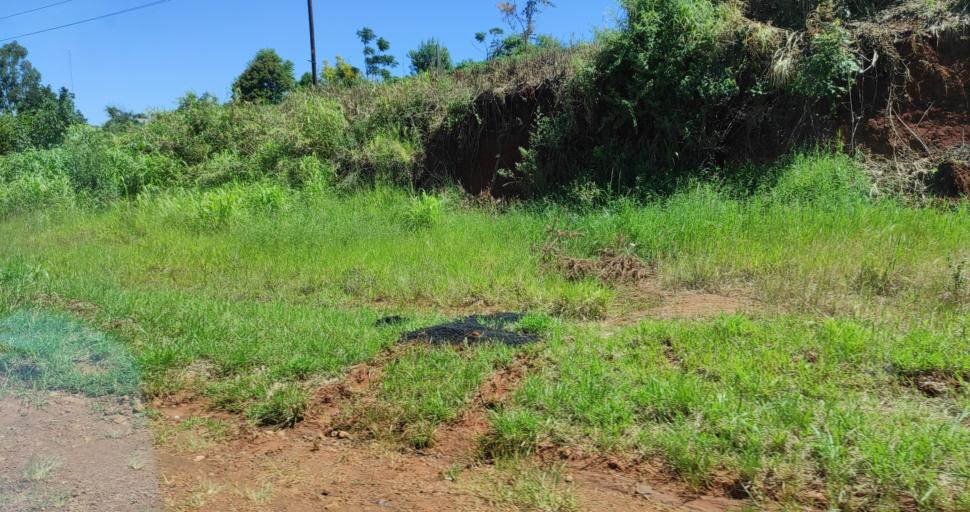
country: AR
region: Misiones
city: El Soberbio
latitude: -27.2857
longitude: -54.2220
